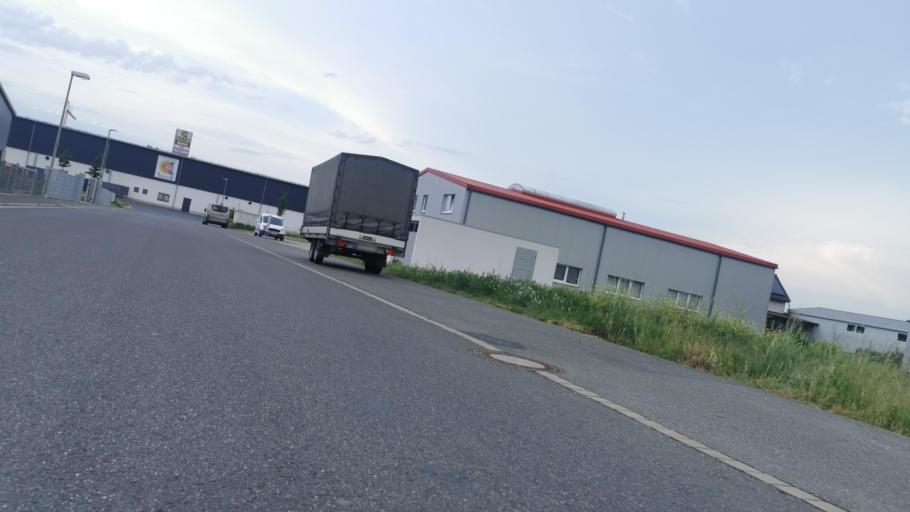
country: DE
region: Bavaria
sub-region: Regierungsbezirk Mittelfranken
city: Gremsdorf
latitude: 49.7044
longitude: 10.8269
